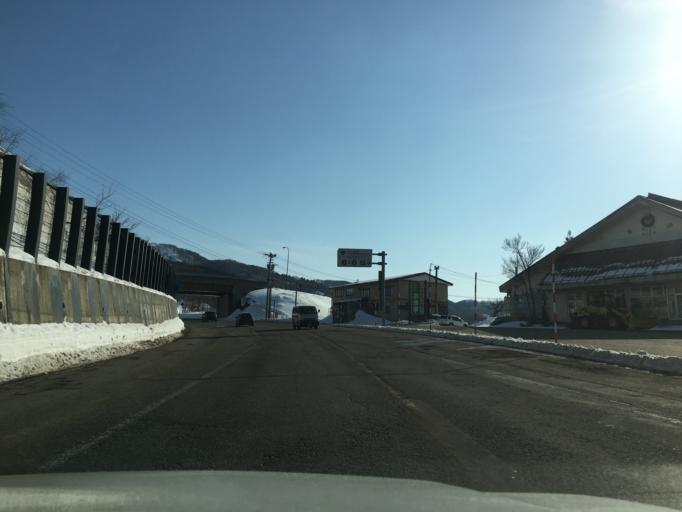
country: JP
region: Yamagata
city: Tsuruoka
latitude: 38.5727
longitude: 139.9383
